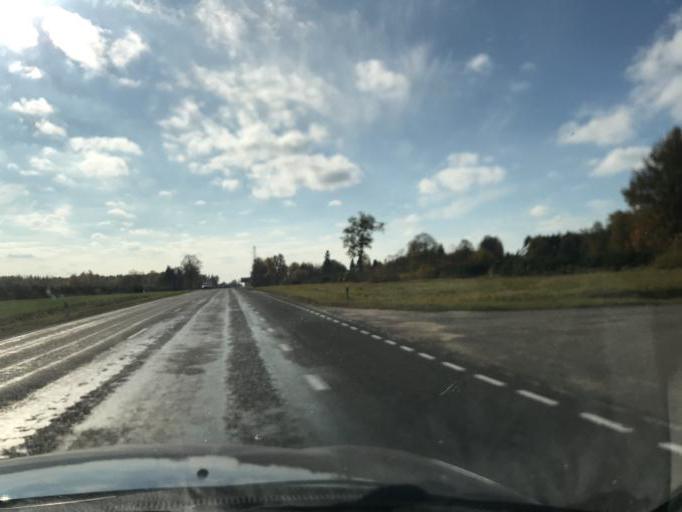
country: BY
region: Grodnenskaya
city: Voranava
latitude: 54.1794
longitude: 25.3348
